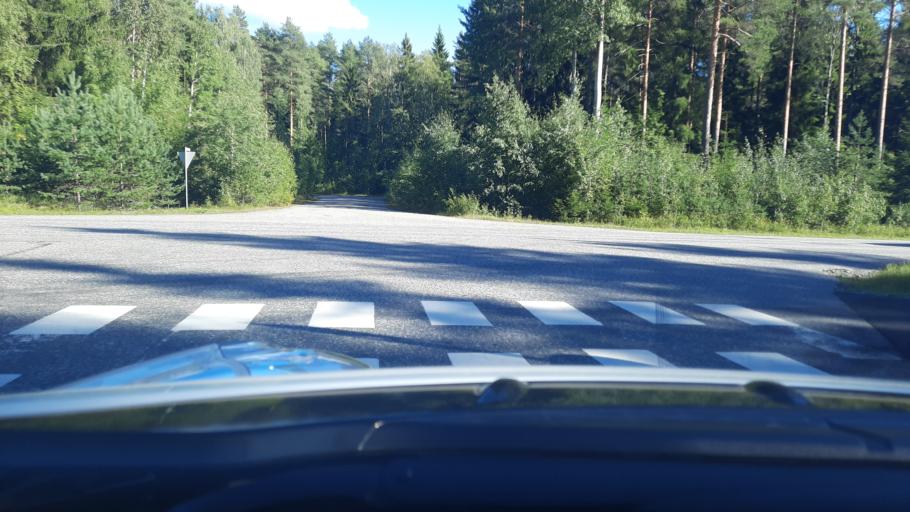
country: FI
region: North Karelia
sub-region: Joensuu
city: Joensuu
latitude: 62.6337
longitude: 29.7003
